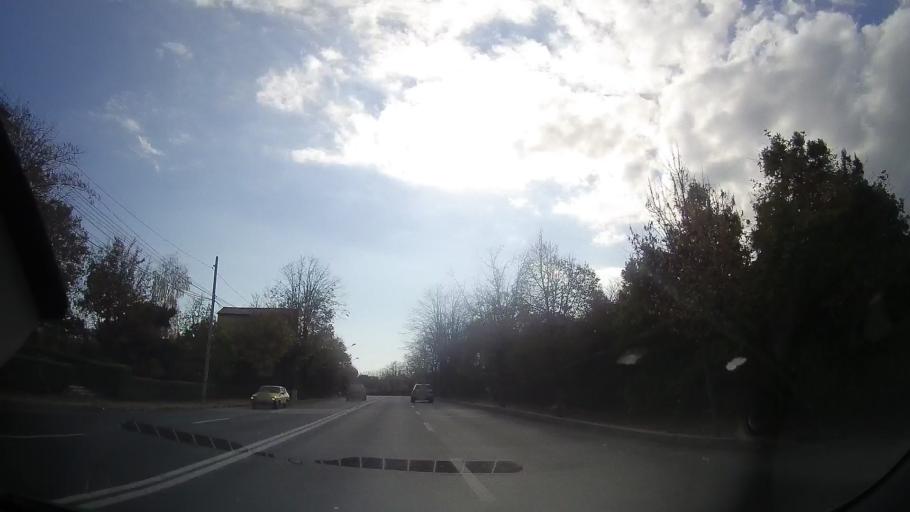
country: RO
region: Constanta
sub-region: Oras Eforie
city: Eforie
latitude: 44.0352
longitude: 28.6461
